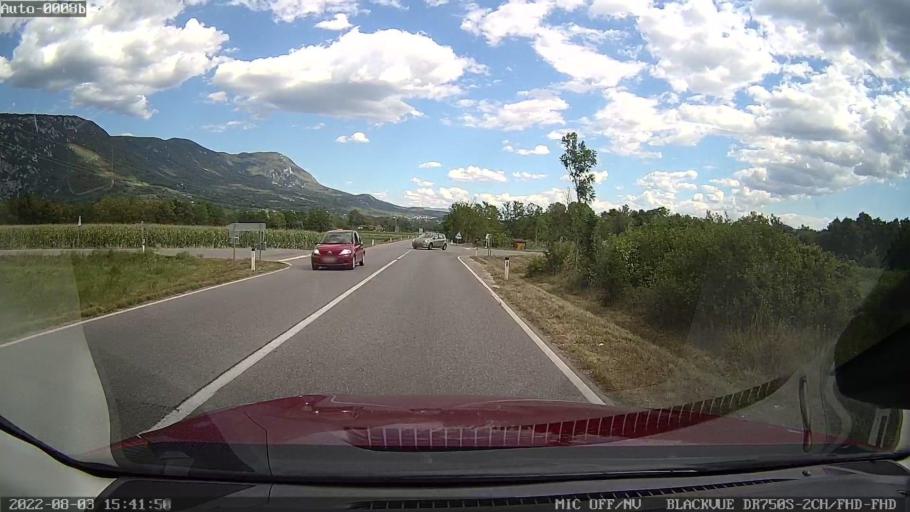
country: SI
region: Sempeter-Vrtojba
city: Rozna Dolina
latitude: 45.9530
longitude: 13.6920
